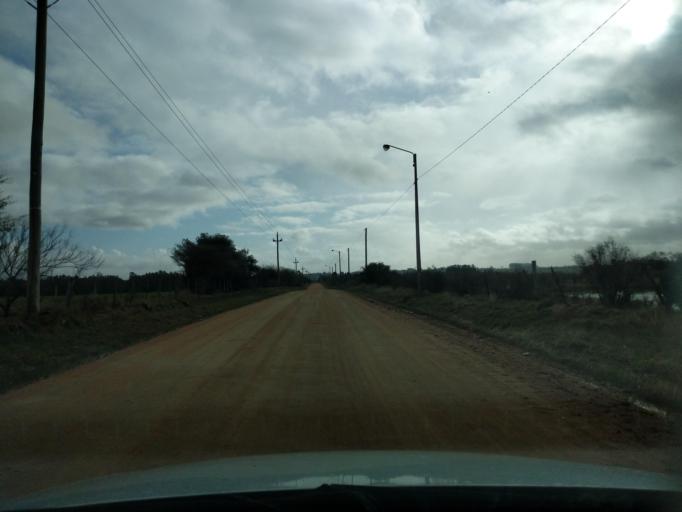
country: UY
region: Florida
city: Florida
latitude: -34.0770
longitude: -56.2225
